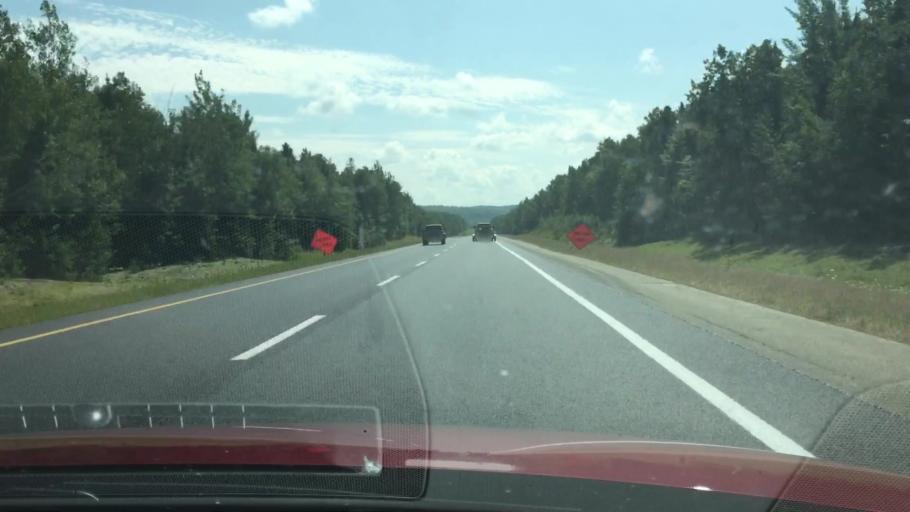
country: US
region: Maine
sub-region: Penobscot County
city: Patten
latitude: 45.8186
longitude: -68.4309
